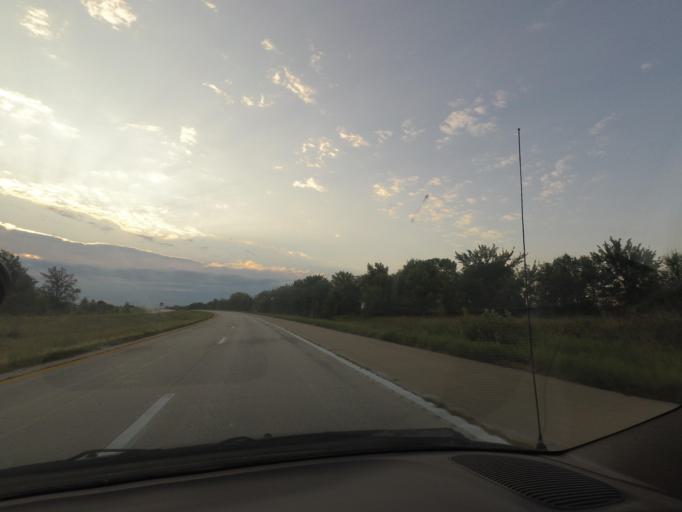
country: US
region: Missouri
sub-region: Shelby County
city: Shelbina
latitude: 39.7408
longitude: -92.2404
